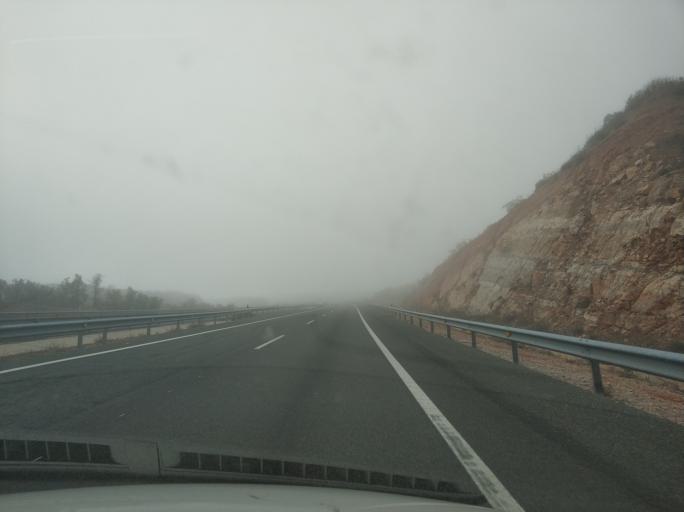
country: ES
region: Castille and Leon
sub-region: Provincia de Soria
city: Adradas
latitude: 41.3181
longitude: -2.4812
